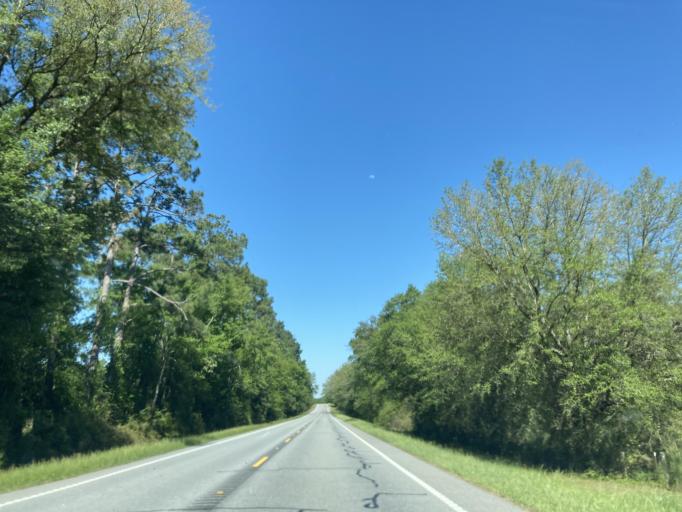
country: US
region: Georgia
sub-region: Miller County
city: Colquitt
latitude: 31.1872
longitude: -84.5279
